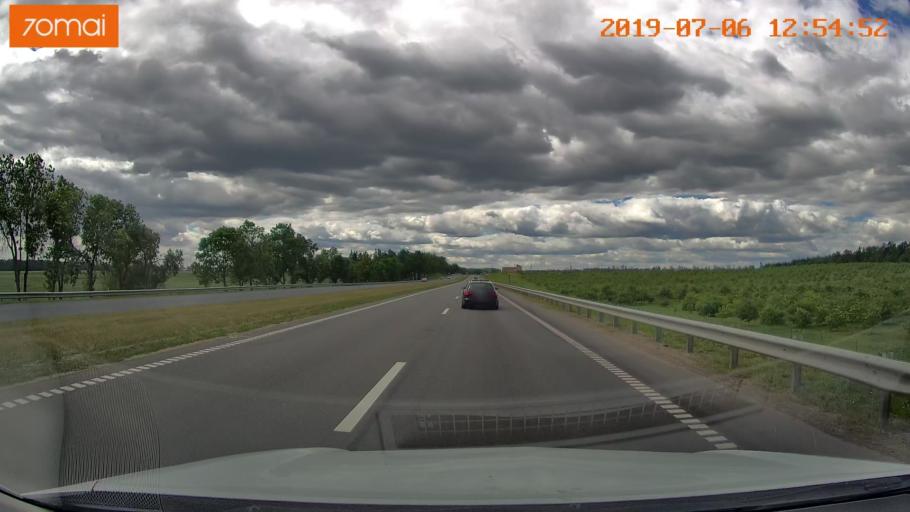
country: BY
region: Minsk
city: Dzyarzhynsk
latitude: 53.6982
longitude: 27.1823
